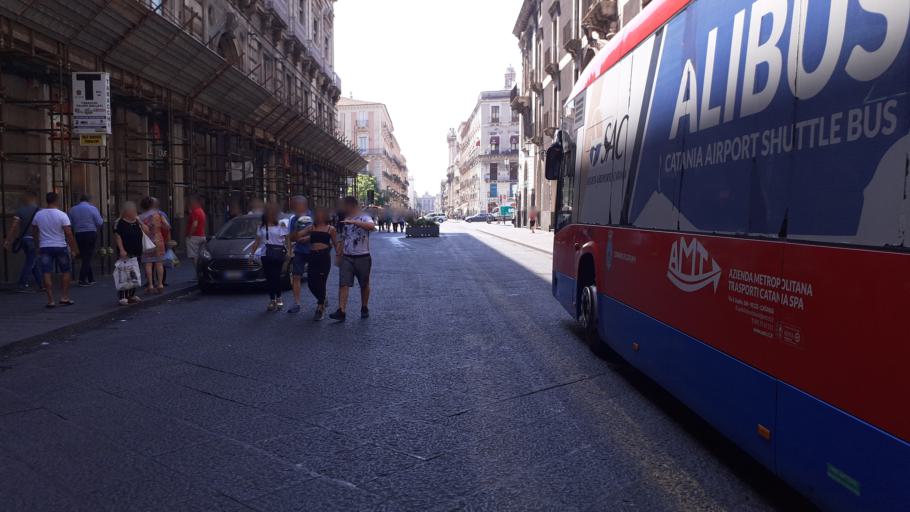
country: IT
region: Sicily
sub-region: Catania
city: Catania
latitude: 37.5083
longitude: 15.0861
